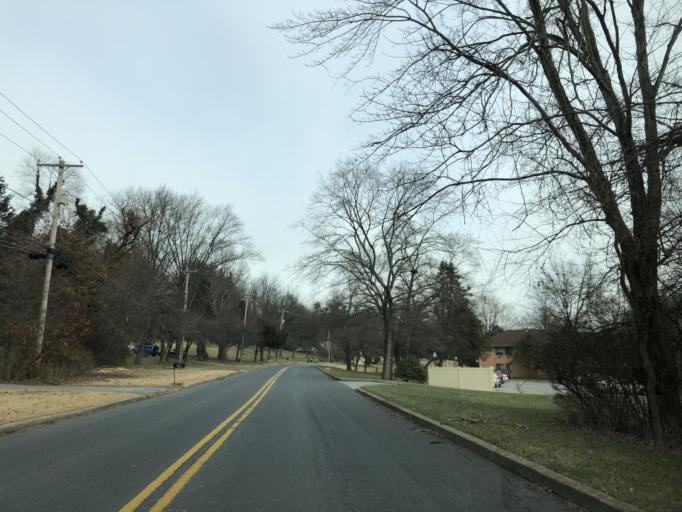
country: US
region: Pennsylvania
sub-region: Chester County
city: Exton
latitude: 40.0380
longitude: -75.6383
